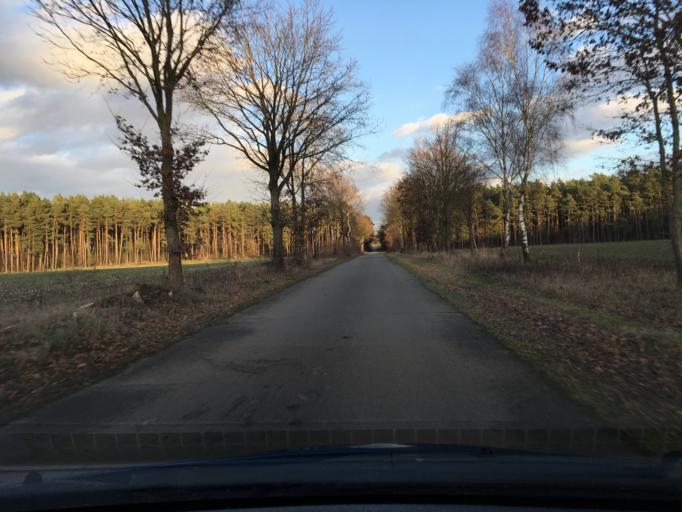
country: DE
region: Lower Saxony
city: Soderstorf
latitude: 53.1103
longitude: 10.1490
